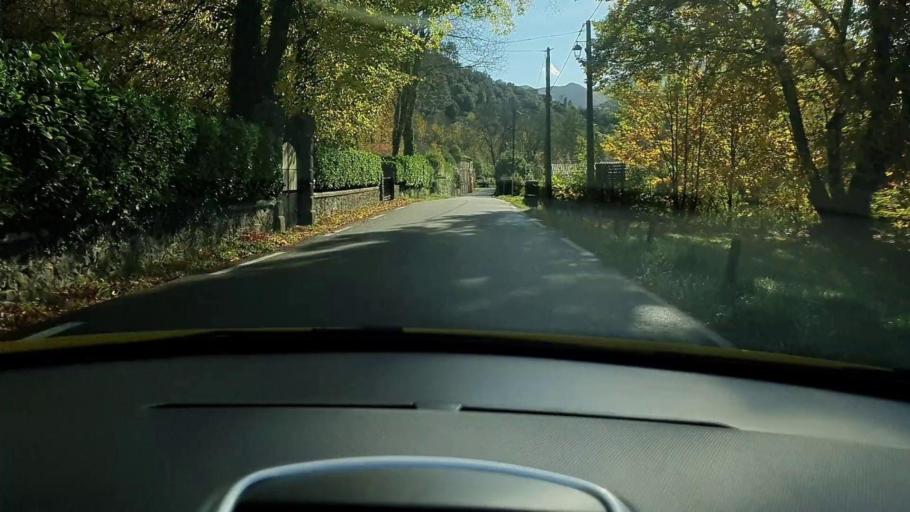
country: FR
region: Languedoc-Roussillon
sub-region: Departement du Gard
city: Lasalle
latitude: 44.1262
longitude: 3.7633
